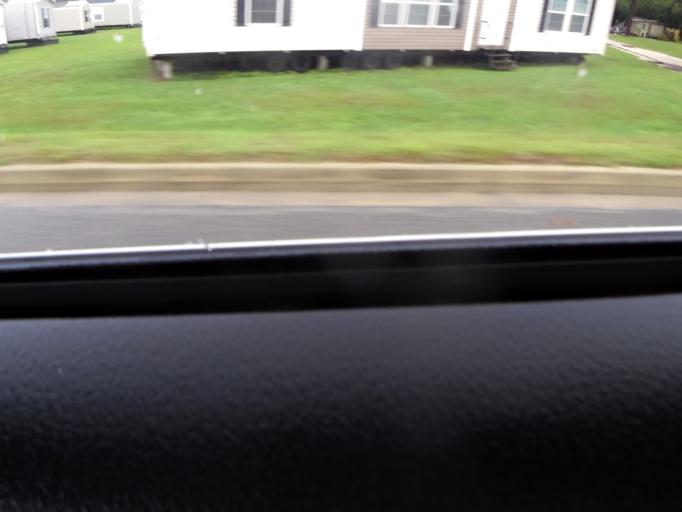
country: US
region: Georgia
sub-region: Wayne County
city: Jesup
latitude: 31.6342
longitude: -81.8626
